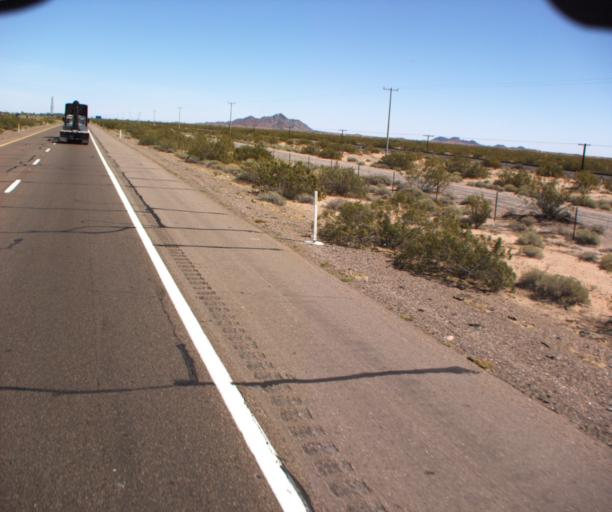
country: US
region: Arizona
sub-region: Yuma County
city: Wellton
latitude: 32.7873
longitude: -113.5650
